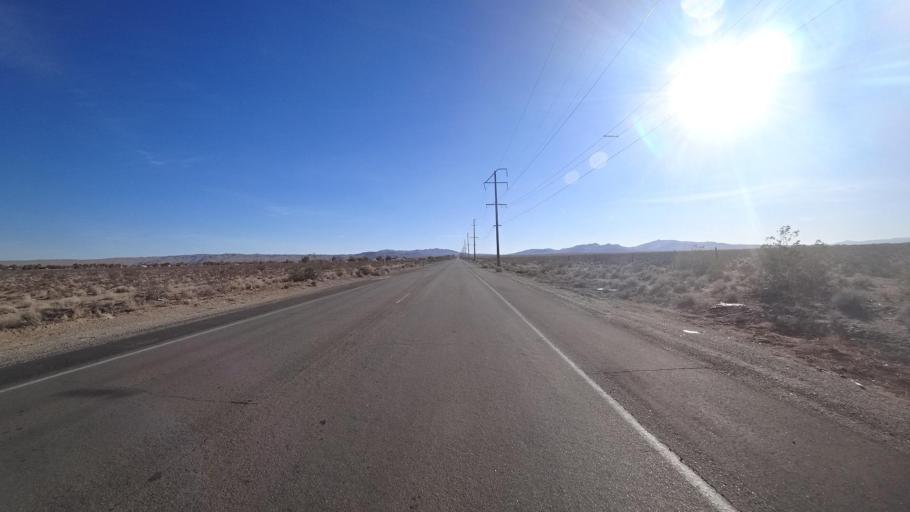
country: US
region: California
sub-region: Kern County
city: China Lake Acres
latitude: 35.6426
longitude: -117.7231
